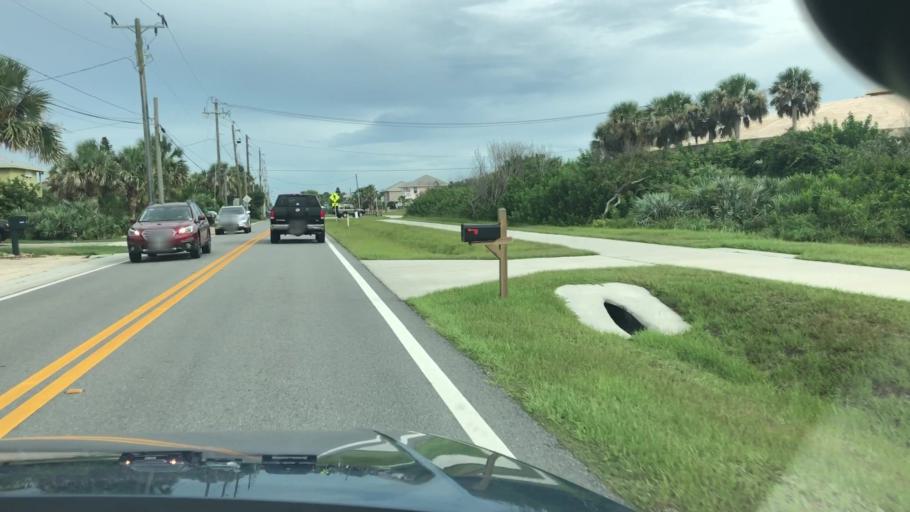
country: US
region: Florida
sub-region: Volusia County
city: Ponce Inlet
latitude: 29.1238
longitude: -80.9535
